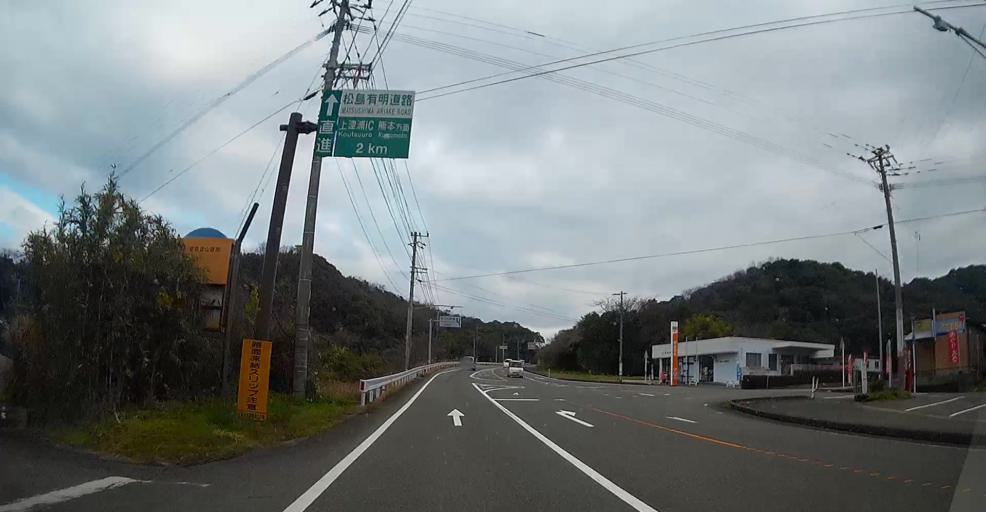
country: JP
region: Kumamoto
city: Hondo
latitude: 32.4928
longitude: 130.2950
